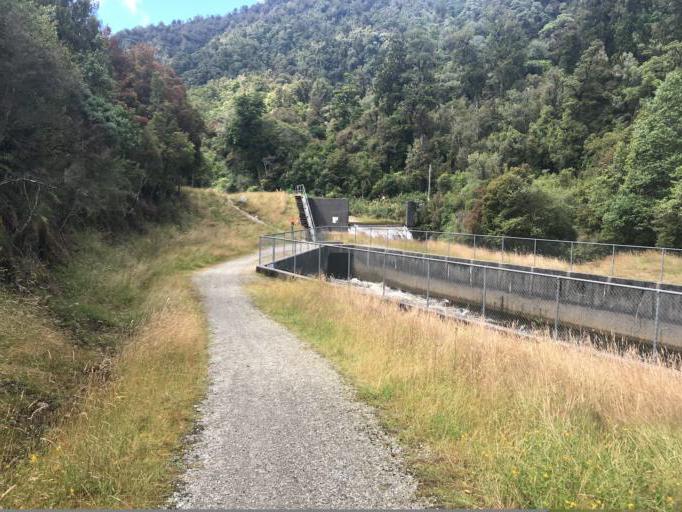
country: NZ
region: West Coast
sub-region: Westland District
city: Hokitika
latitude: -42.7554
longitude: 171.2250
